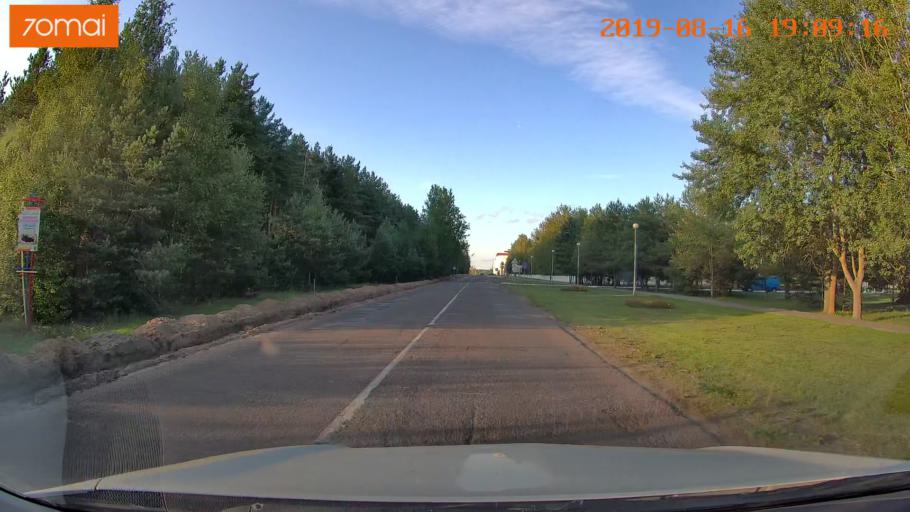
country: BY
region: Mogilev
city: Asipovichy
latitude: 53.3168
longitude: 28.6334
